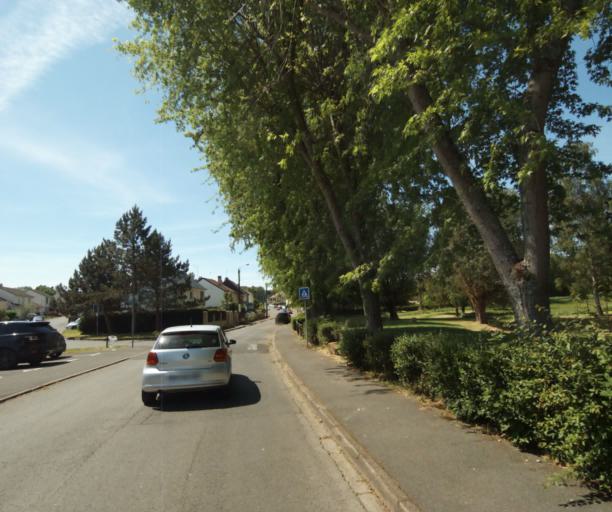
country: FR
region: Champagne-Ardenne
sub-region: Departement des Ardennes
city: La Francheville
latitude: 49.7444
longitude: 4.7143
